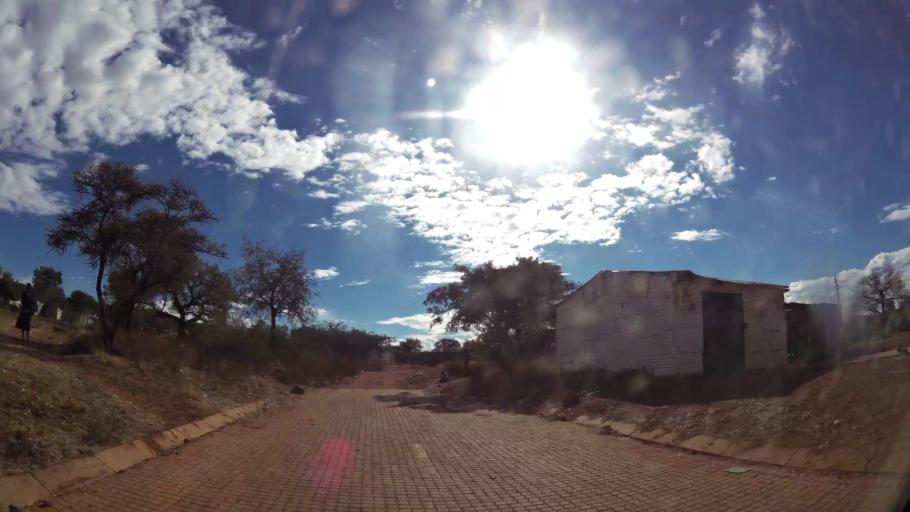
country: ZA
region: Limpopo
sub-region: Waterberg District Municipality
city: Warmbaths
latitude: -24.8750
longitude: 28.2736
